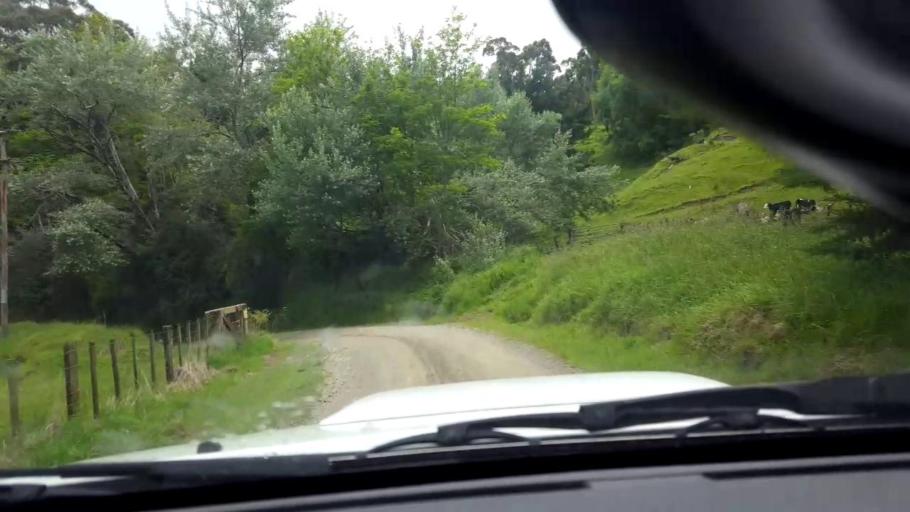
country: NZ
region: Gisborne
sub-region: Gisborne District
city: Gisborne
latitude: -38.3839
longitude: 177.6295
